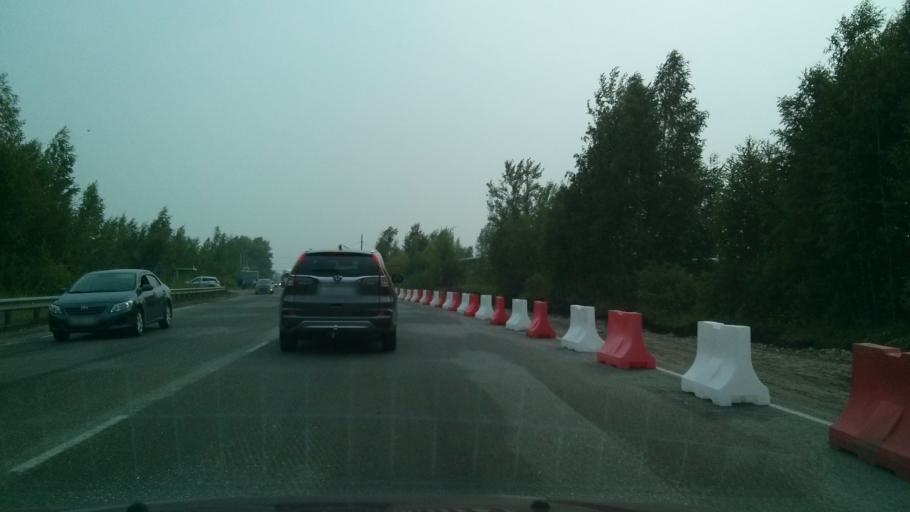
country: RU
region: Nizjnij Novgorod
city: Kstovo
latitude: 56.1215
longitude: 44.1569
